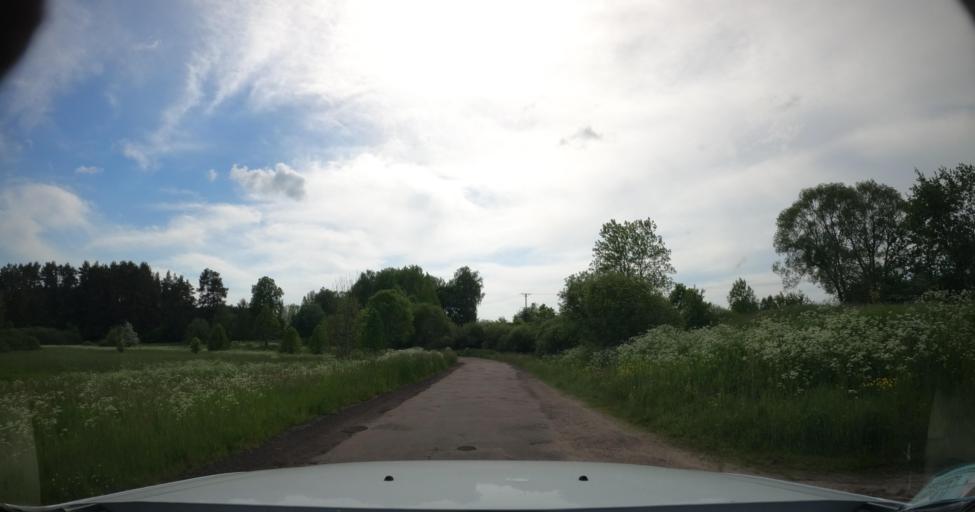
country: PL
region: Warmian-Masurian Voivodeship
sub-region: Powiat lidzbarski
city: Lidzbark Warminski
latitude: 54.1083
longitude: 20.4654
